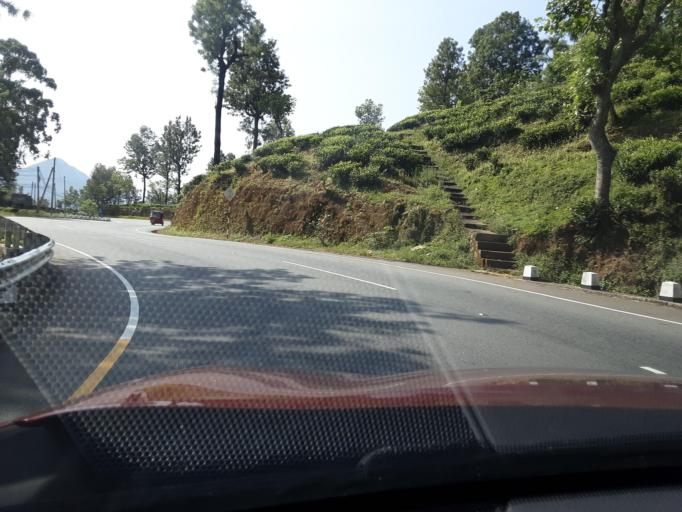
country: LK
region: Uva
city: Badulla
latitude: 6.9521
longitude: 81.1224
